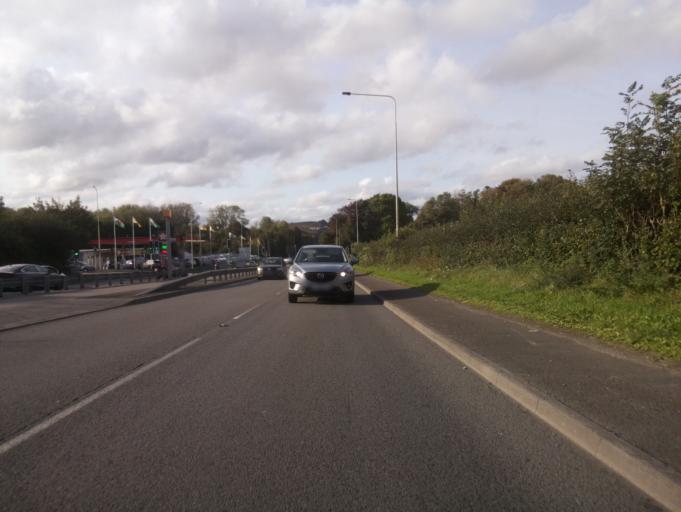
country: GB
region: Wales
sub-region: Rhondda Cynon Taf
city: Llantrisant
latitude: 51.5234
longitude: -3.3629
